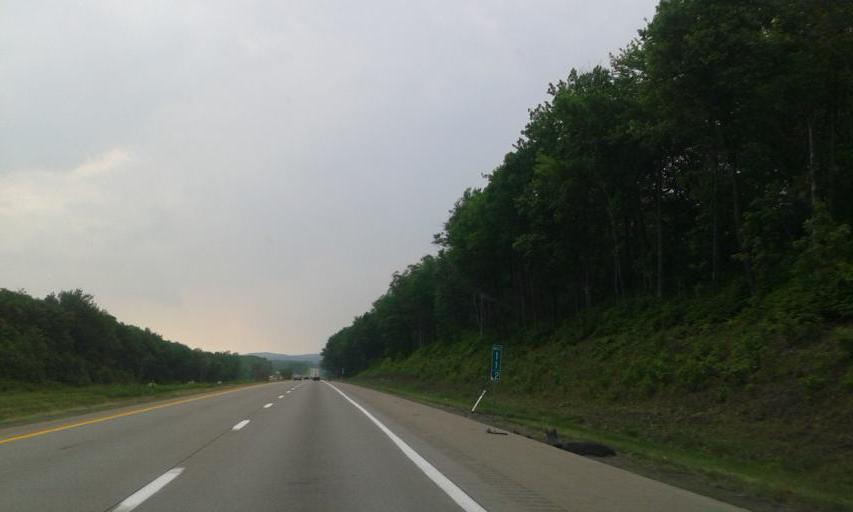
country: US
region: Pennsylvania
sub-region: Monroe County
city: Pocono Pines
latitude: 41.2127
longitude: -75.4713
